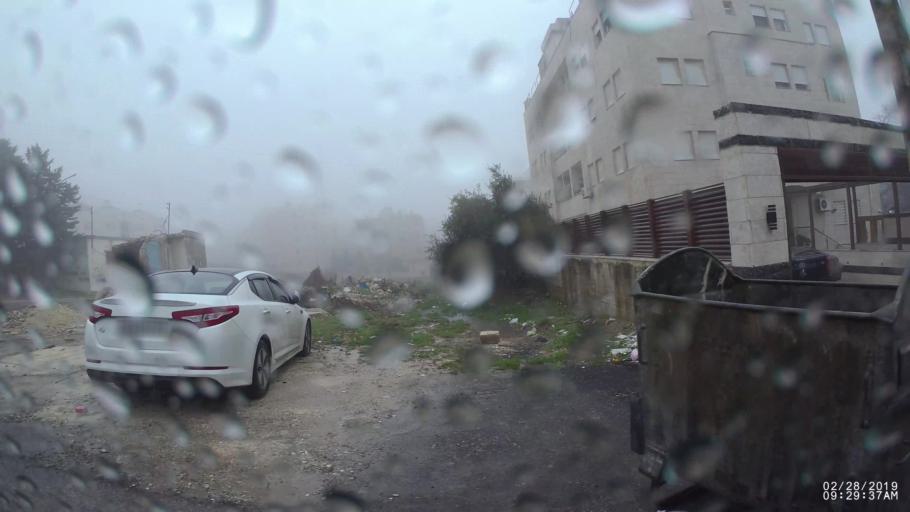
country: JO
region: Amman
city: Al Jubayhah
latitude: 32.0077
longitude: 35.8799
